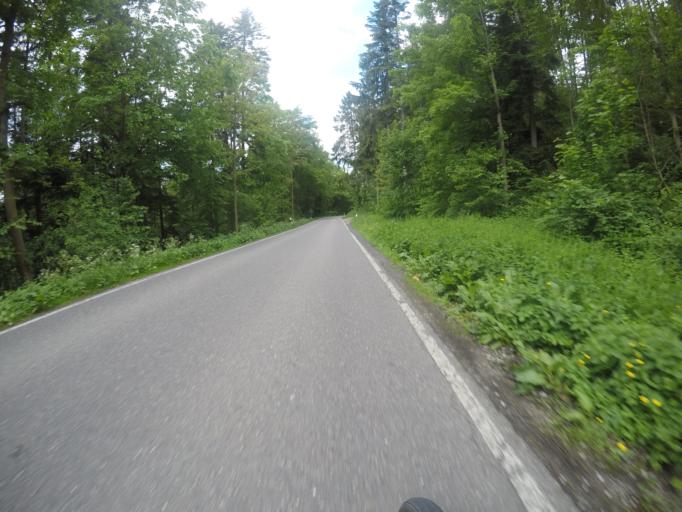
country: DE
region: Baden-Wuerttemberg
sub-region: Regierungsbezirk Stuttgart
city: Oberjettingen
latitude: 48.5803
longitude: 8.7425
